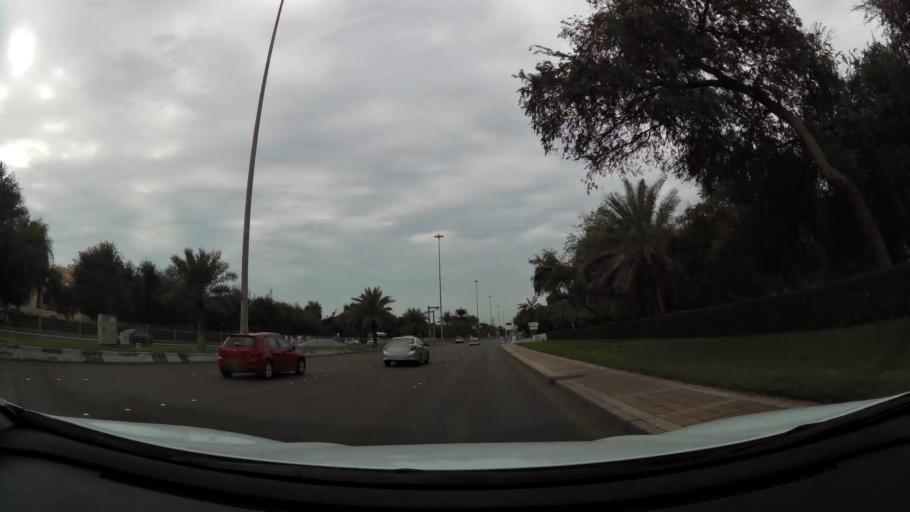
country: AE
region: Abu Dhabi
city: Abu Dhabi
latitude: 24.4394
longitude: 54.4001
